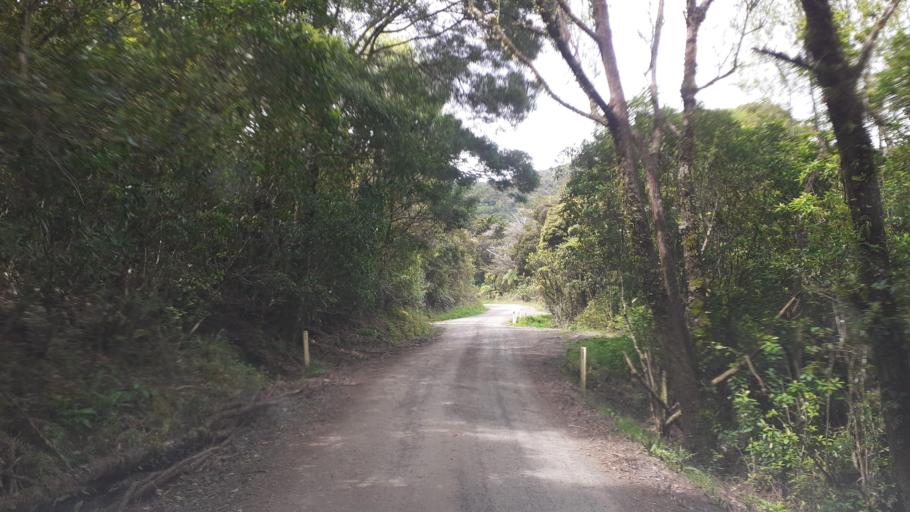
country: NZ
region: Northland
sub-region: Far North District
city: Waimate North
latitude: -35.5747
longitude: 173.5692
